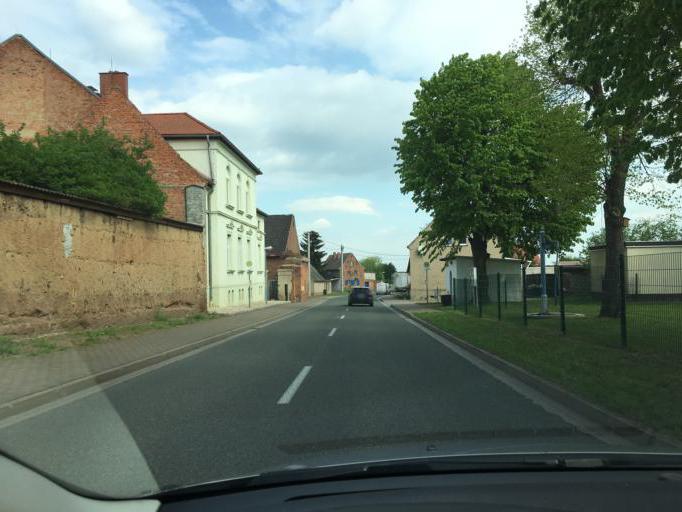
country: DE
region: Saxony-Anhalt
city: Grobzig
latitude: 51.6623
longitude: 11.8401
